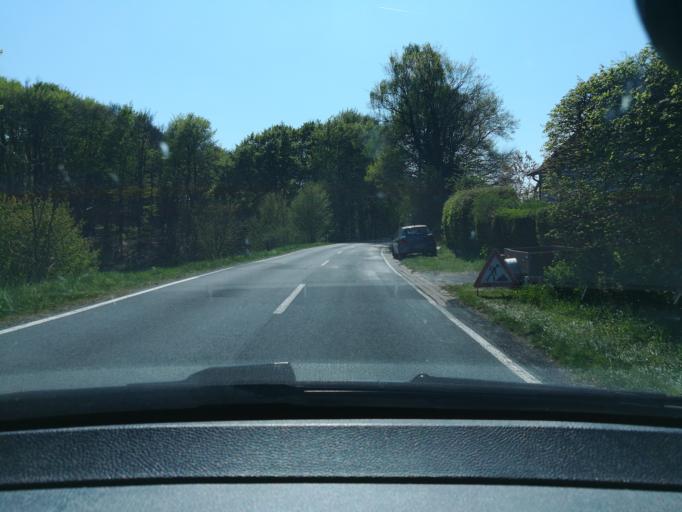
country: DE
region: North Rhine-Westphalia
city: Halle
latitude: 52.0478
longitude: 8.3938
